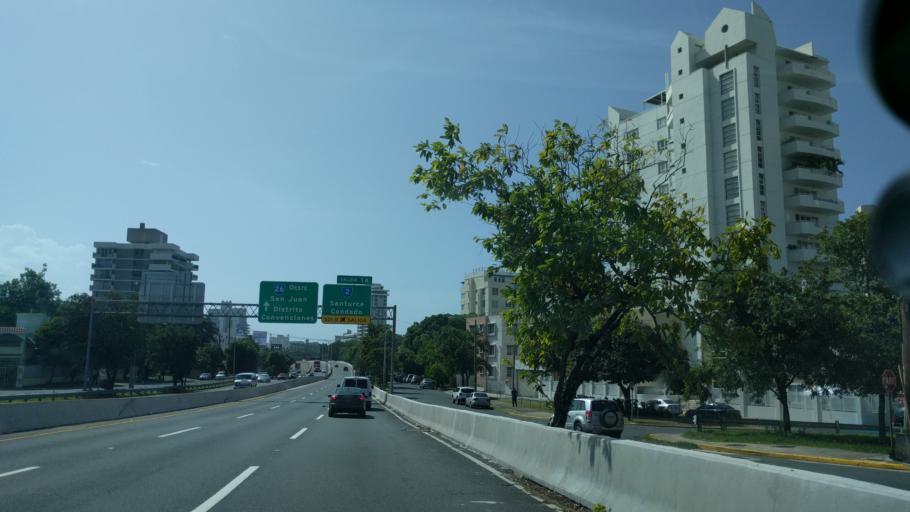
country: PR
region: San Juan
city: San Juan
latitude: 18.4517
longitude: -66.0697
